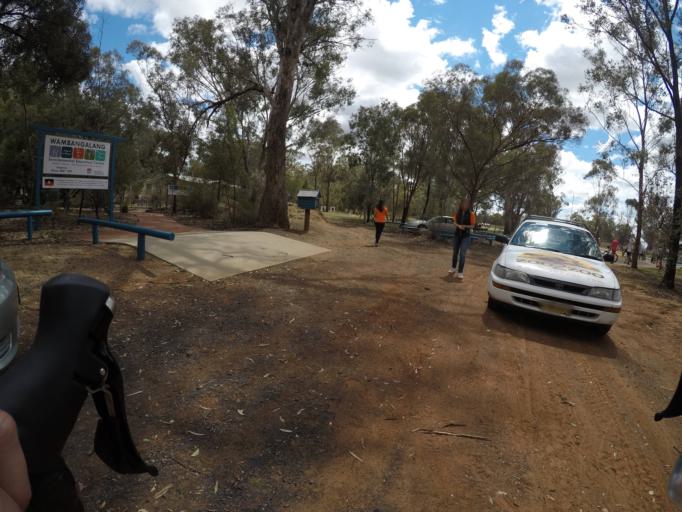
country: AU
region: New South Wales
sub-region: Dubbo Municipality
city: Dubbo
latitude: -32.4882
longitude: 148.5555
